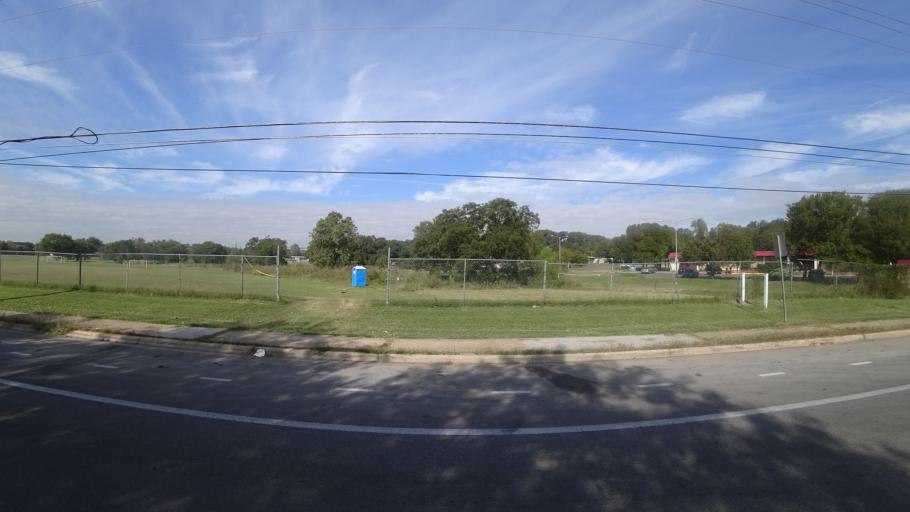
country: US
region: Texas
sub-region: Travis County
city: Austin
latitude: 30.2721
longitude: -97.6994
